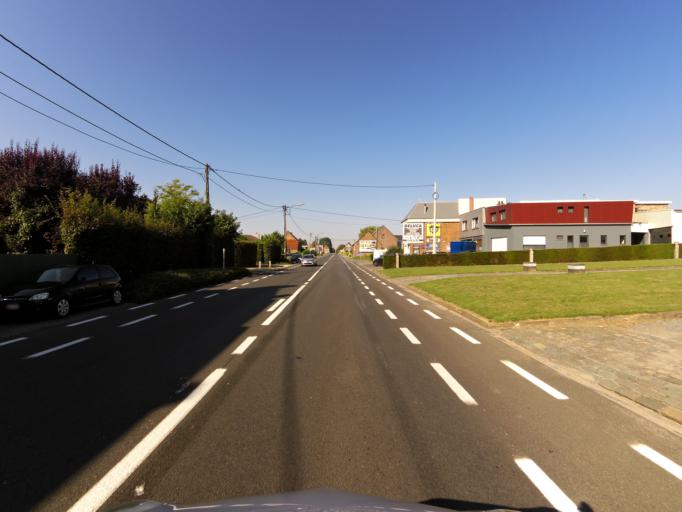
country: BE
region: Flanders
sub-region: Provincie Oost-Vlaanderen
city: Sint-Maria-Lierde
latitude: 50.8110
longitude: 3.7989
